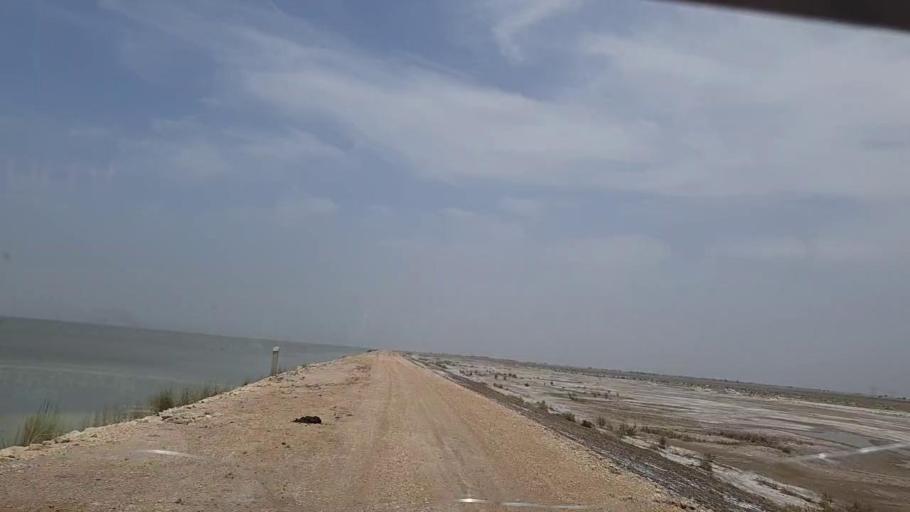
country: PK
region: Sindh
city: Sehwan
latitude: 26.4120
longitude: 67.7874
